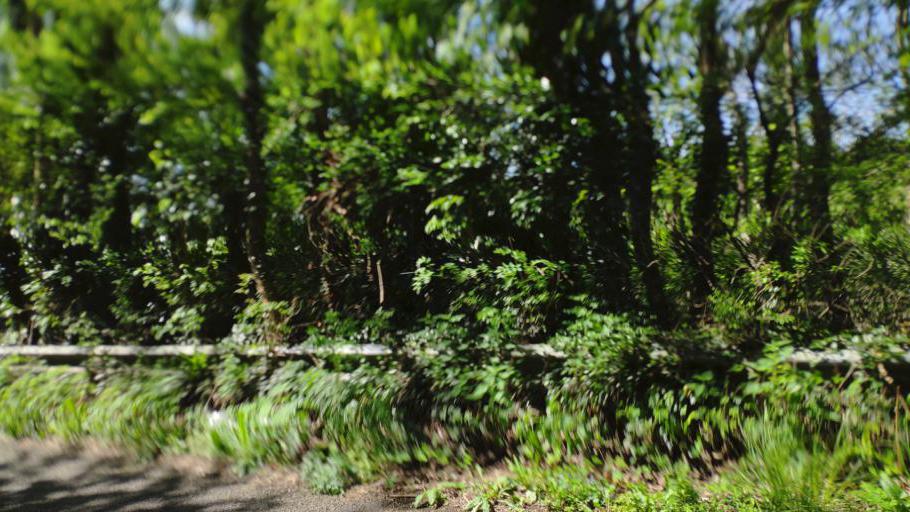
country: IE
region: Munster
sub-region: County Cork
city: Blarney
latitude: 51.9608
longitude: -8.5766
